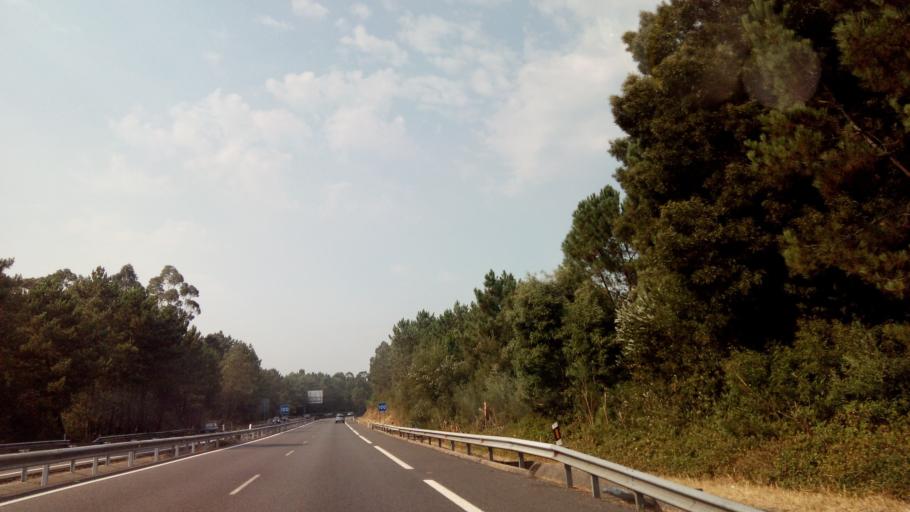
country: ES
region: Galicia
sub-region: Provincia de Pontevedra
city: Tui
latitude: 42.0744
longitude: -8.6321
